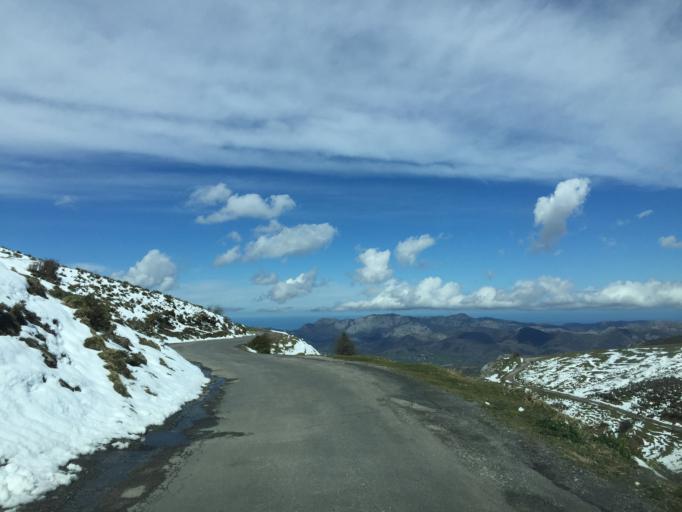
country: ES
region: Asturias
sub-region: Province of Asturias
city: Amieva
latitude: 43.2746
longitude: -4.9828
